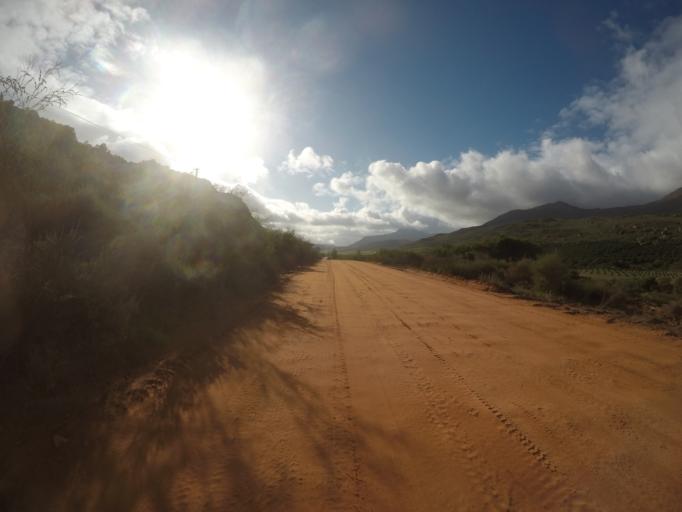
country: ZA
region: Western Cape
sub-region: West Coast District Municipality
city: Clanwilliam
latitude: -32.3429
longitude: 18.8105
